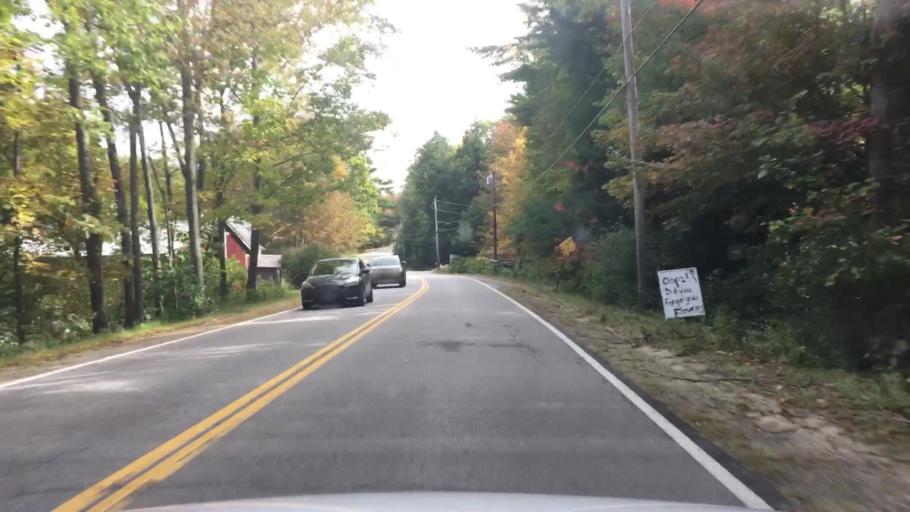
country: US
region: Maine
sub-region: Sagadahoc County
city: Topsham
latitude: 43.9376
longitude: -70.0214
